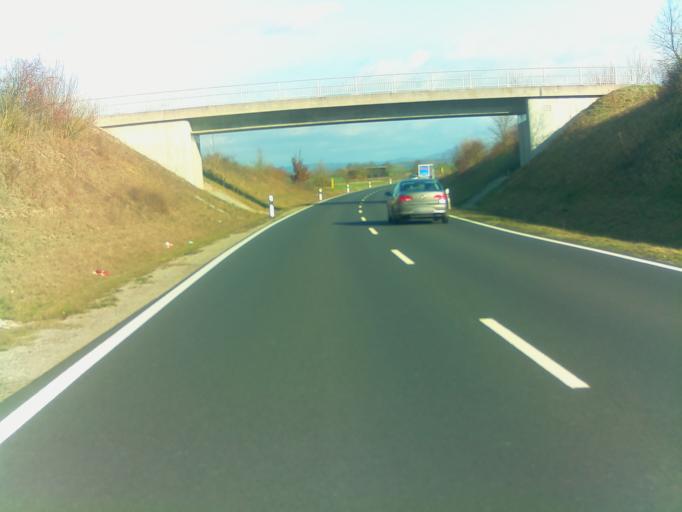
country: DE
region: Bavaria
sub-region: Regierungsbezirk Unterfranken
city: Bad Konigshofen im Grabfeld
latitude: 50.3037
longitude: 10.4472
